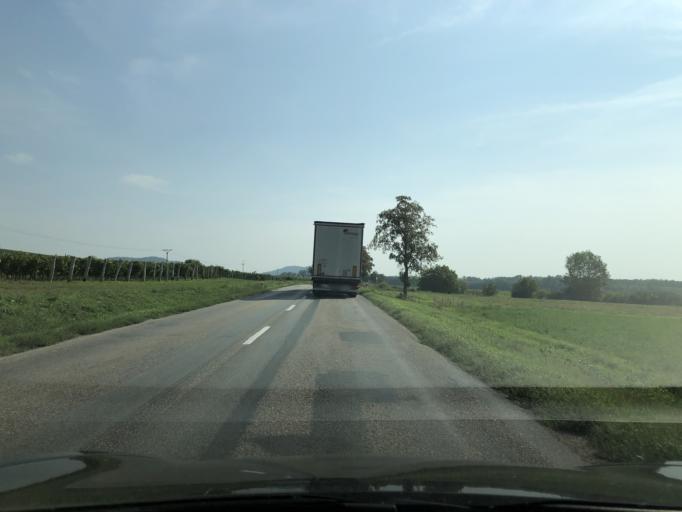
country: CZ
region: South Moravian
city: Brezi
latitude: 48.8202
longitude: 16.5791
